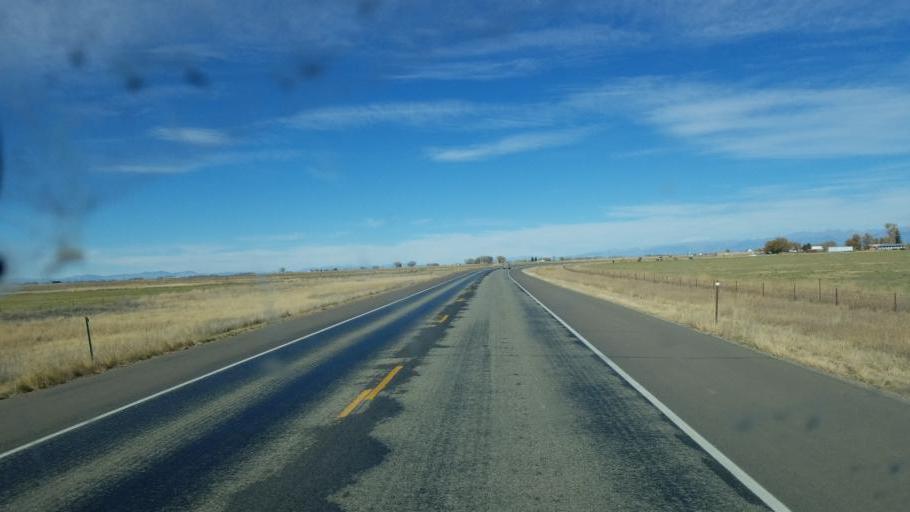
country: US
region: Colorado
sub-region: Alamosa County
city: Alamosa
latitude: 37.3597
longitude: -105.9290
